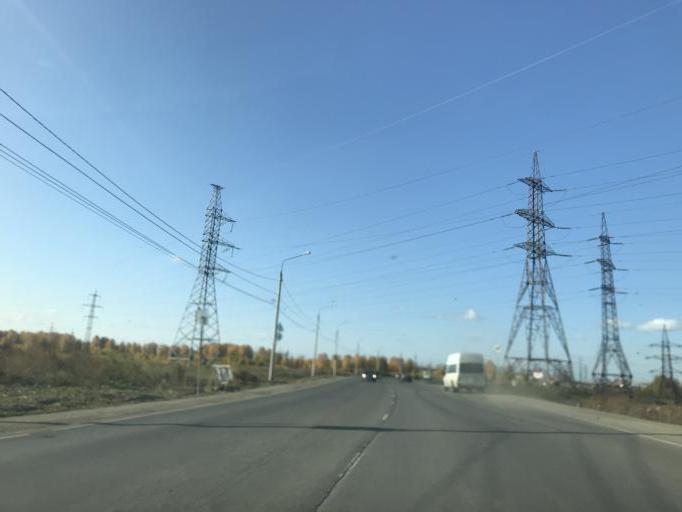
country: RU
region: Chelyabinsk
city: Roshchino
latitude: 55.2248
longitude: 61.2909
